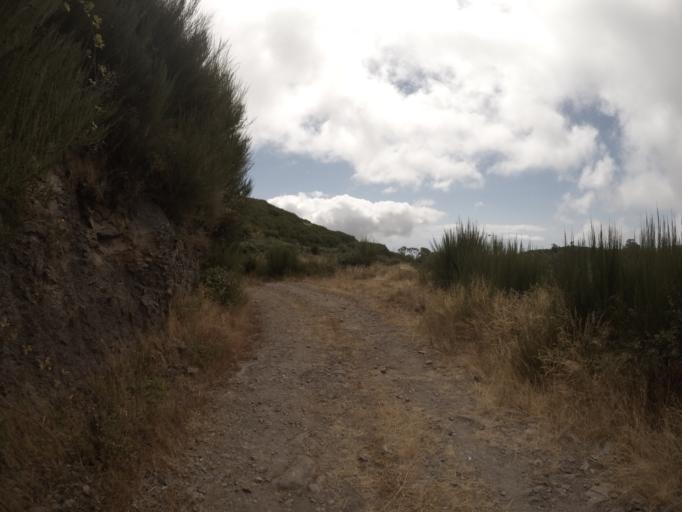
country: PT
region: Madeira
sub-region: Camara de Lobos
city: Curral das Freiras
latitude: 32.7136
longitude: -16.9943
